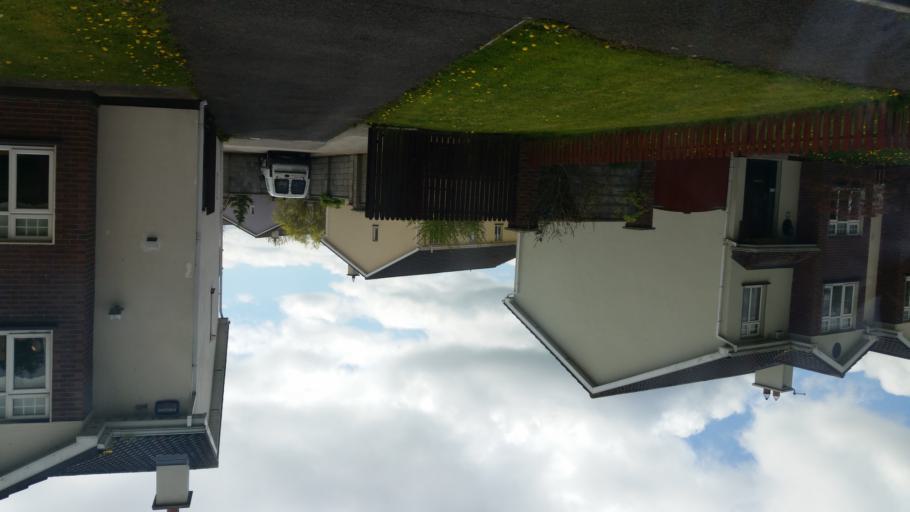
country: IE
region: Leinster
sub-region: Laois
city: Portlaoise
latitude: 53.0463
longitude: -7.3114
